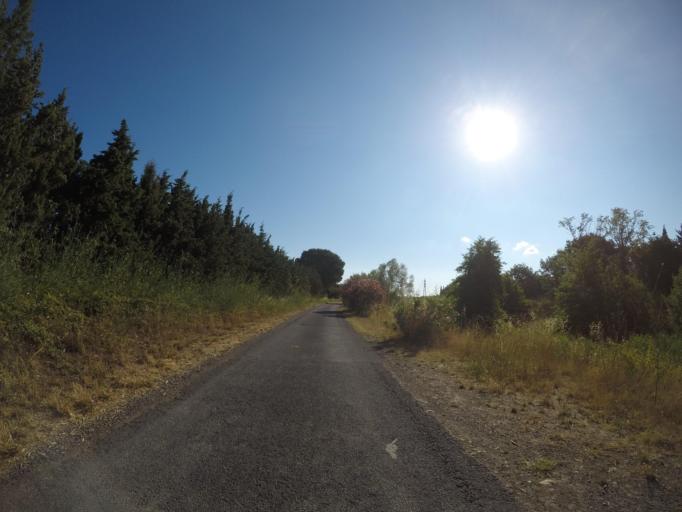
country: FR
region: Languedoc-Roussillon
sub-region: Departement des Pyrenees-Orientales
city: Pezilla-la-Riviere
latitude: 42.6776
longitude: 2.7699
